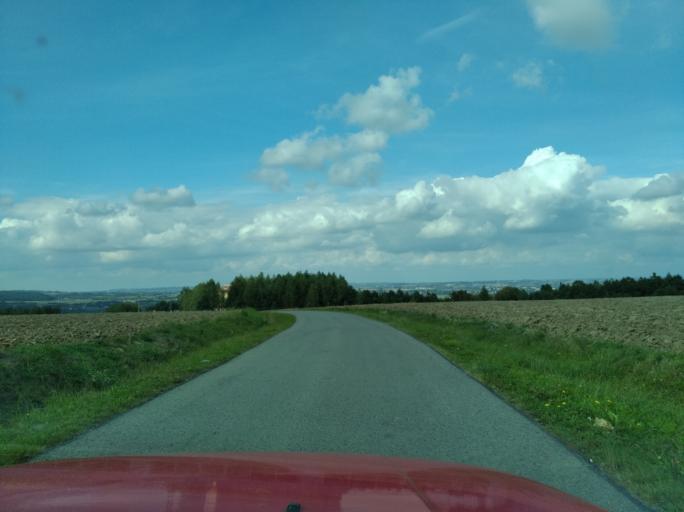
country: PL
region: Subcarpathian Voivodeship
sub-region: Powiat rzeszowski
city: Lubenia
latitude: 49.9364
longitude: 21.9429
